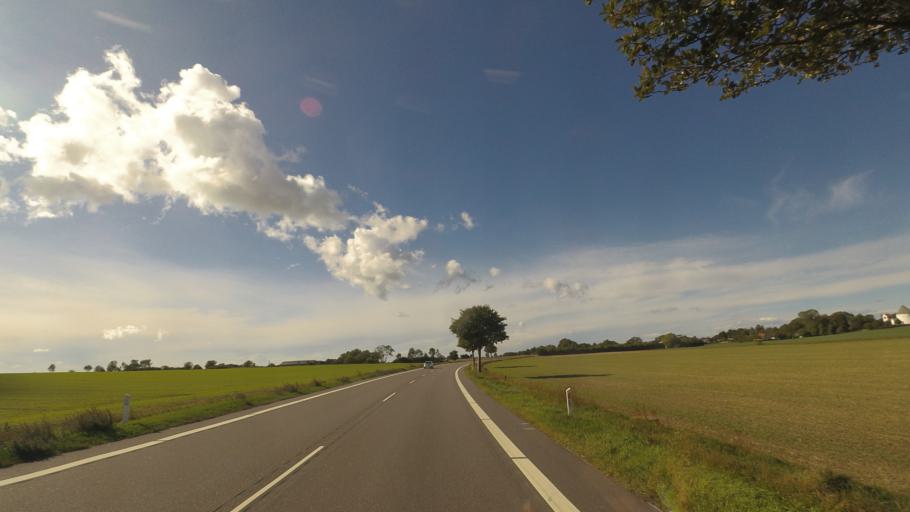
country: DK
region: Capital Region
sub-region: Bornholm Kommune
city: Akirkeby
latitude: 55.0693
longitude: 14.8216
